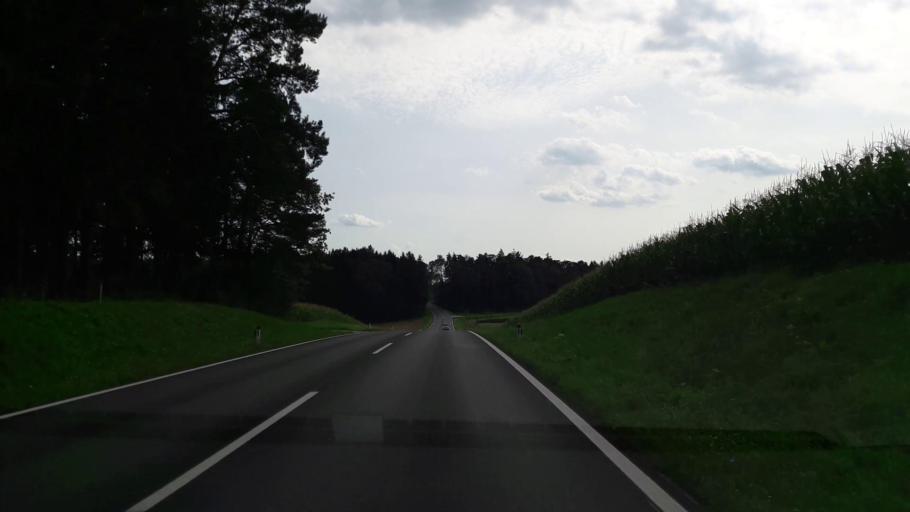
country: AT
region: Styria
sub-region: Politischer Bezirk Hartberg-Fuerstenfeld
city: Hartberg
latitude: 47.2582
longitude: 15.9388
